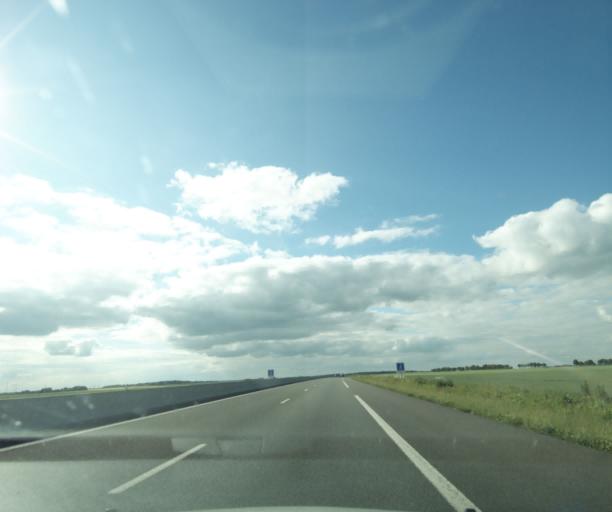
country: FR
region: Centre
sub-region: Departement d'Eure-et-Loir
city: Sours
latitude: 48.3681
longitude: 1.5939
